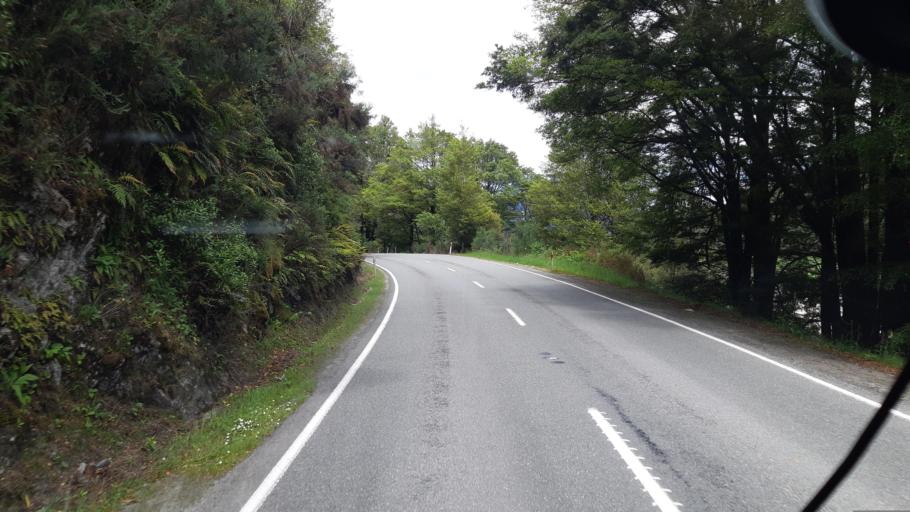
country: NZ
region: West Coast
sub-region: Buller District
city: Westport
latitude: -42.1558
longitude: 171.9137
